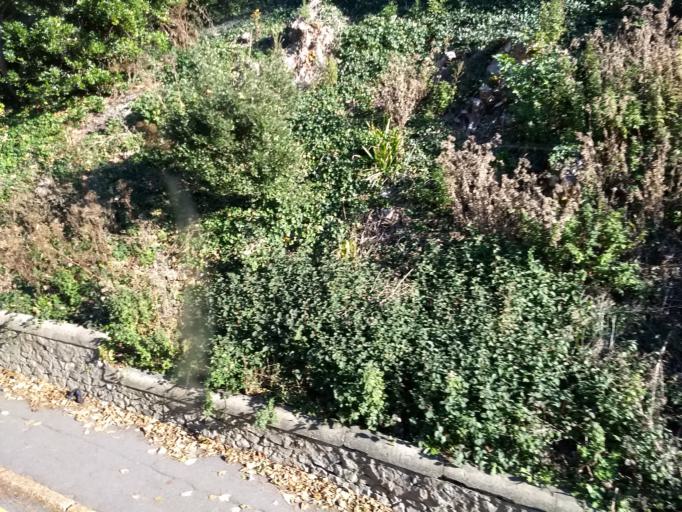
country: GB
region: England
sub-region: Isle of Wight
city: Ventnor
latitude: 50.5972
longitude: -1.1973
